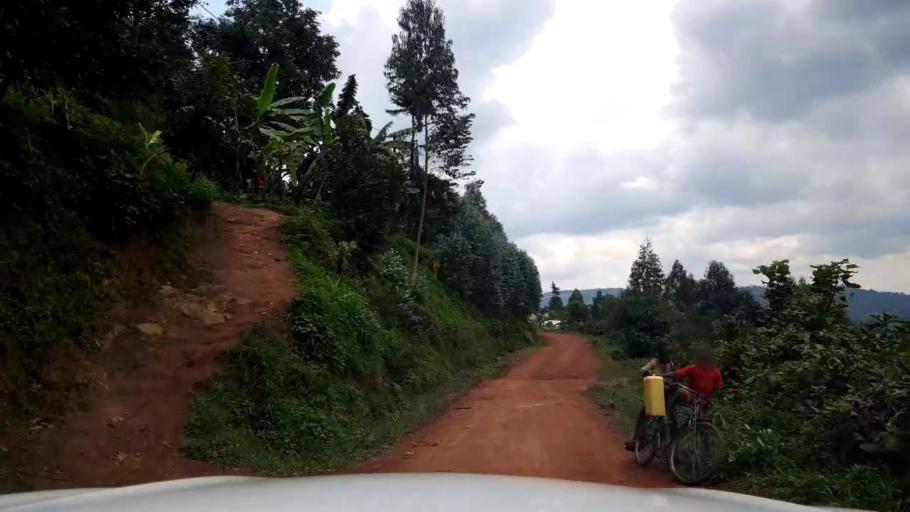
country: RW
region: Northern Province
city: Byumba
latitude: -1.4811
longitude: 29.9070
